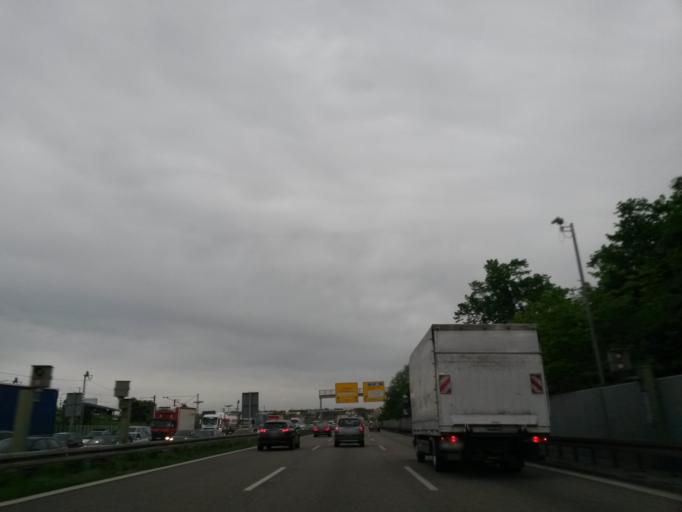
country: DE
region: Baden-Wuerttemberg
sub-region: Regierungsbezirk Stuttgart
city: Stuttgart Feuerbach
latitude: 48.8280
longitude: 9.1689
